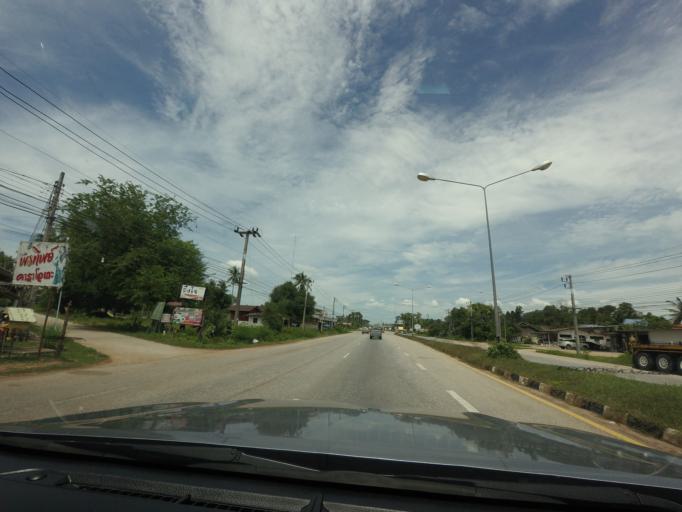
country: TH
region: Songkhla
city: Singhanakhon
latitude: 7.2427
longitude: 100.5446
